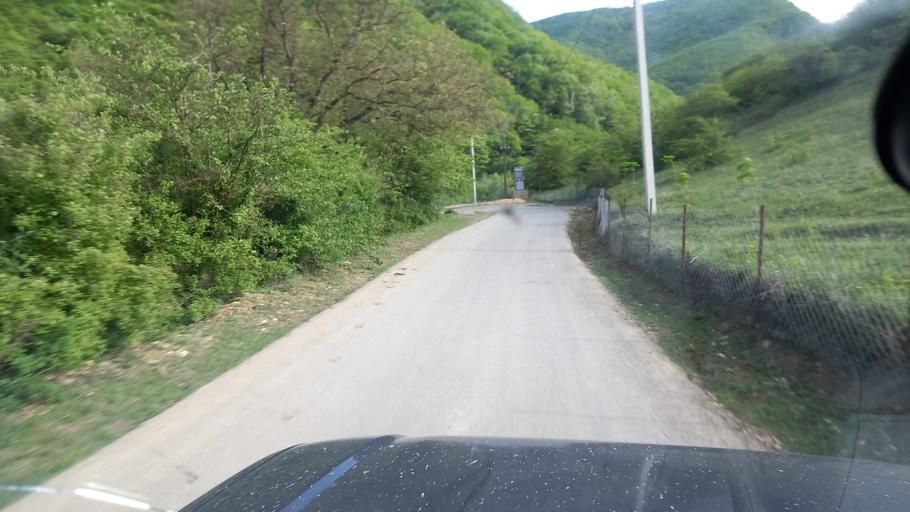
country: RU
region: Dagestan
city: Khuchni
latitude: 41.9655
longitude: 47.9585
